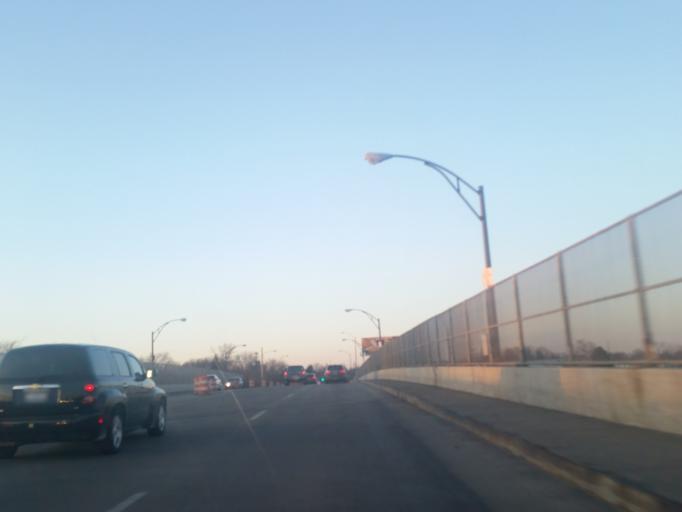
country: US
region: Ohio
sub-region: Cuyahoga County
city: Lakewood
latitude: 41.4458
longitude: -81.8014
